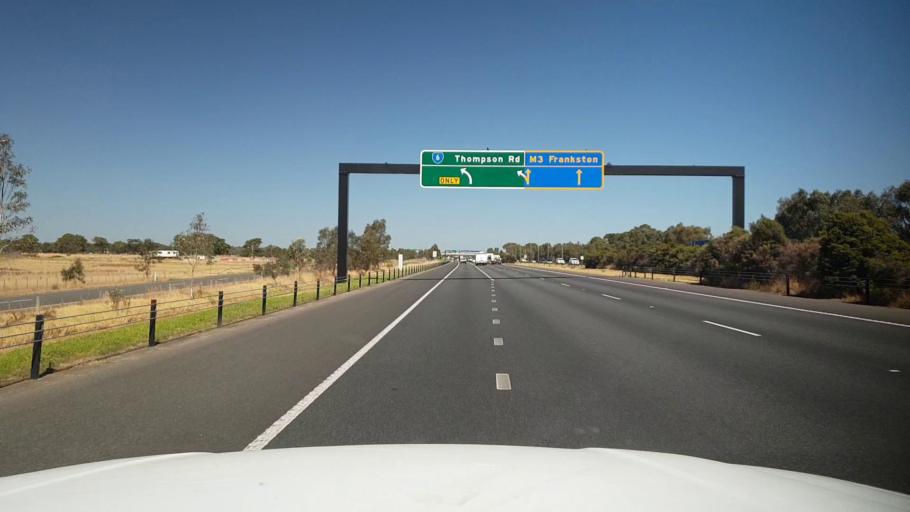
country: AU
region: Victoria
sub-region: Frankston
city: Sandhurst
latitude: -38.0611
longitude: 145.1837
